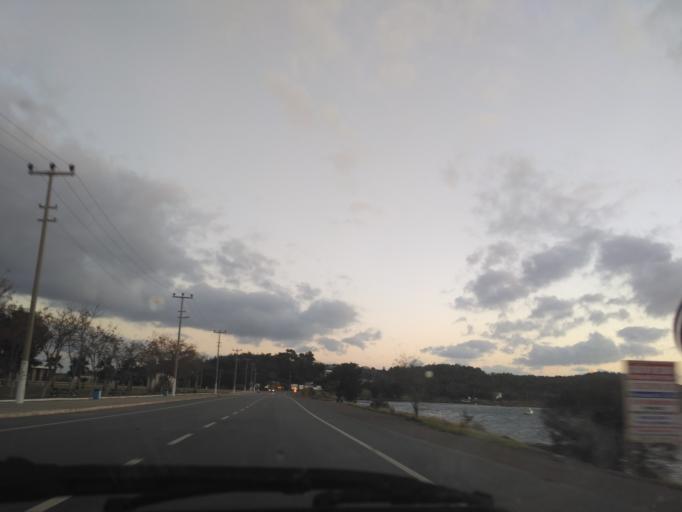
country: TR
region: Balikesir
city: Ayvalik
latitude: 39.2866
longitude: 26.6726
